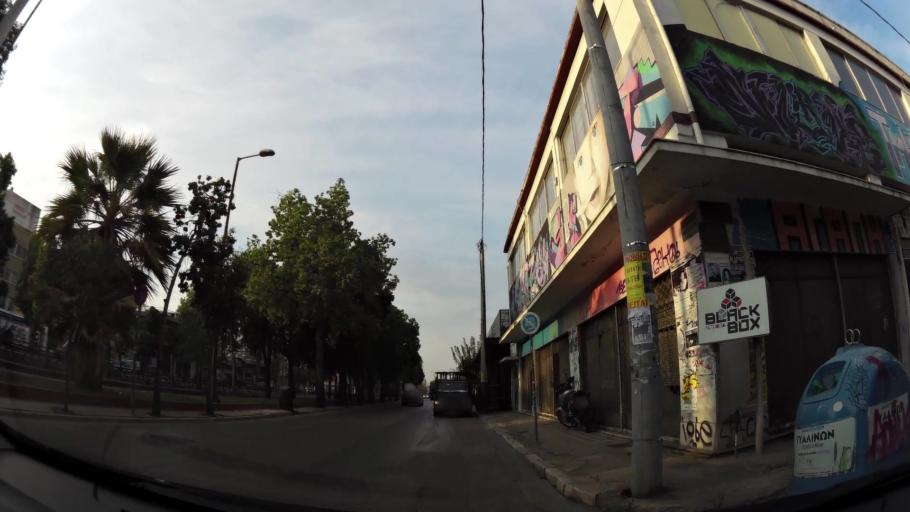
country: GR
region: Attica
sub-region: Nomarchia Athinas
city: Athens
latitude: 37.9820
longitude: 23.7123
